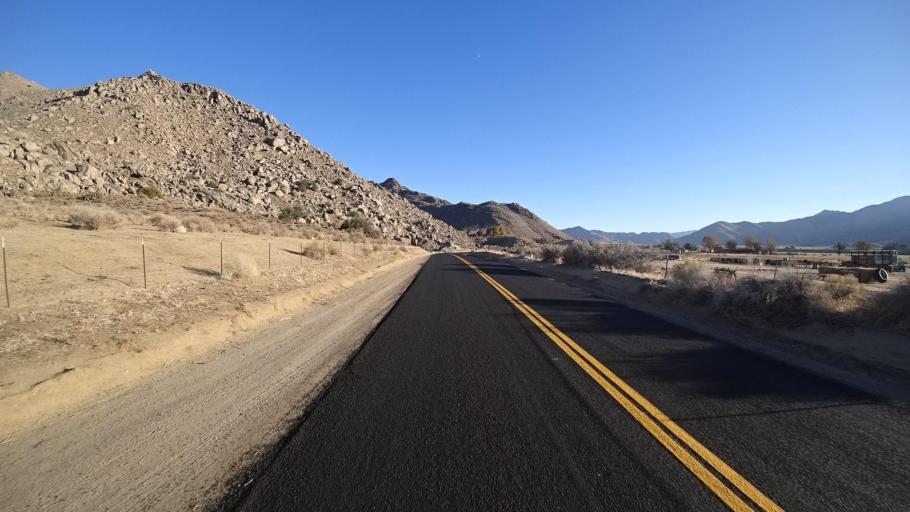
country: US
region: California
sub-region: Kern County
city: Weldon
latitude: 35.6586
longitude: -118.2553
